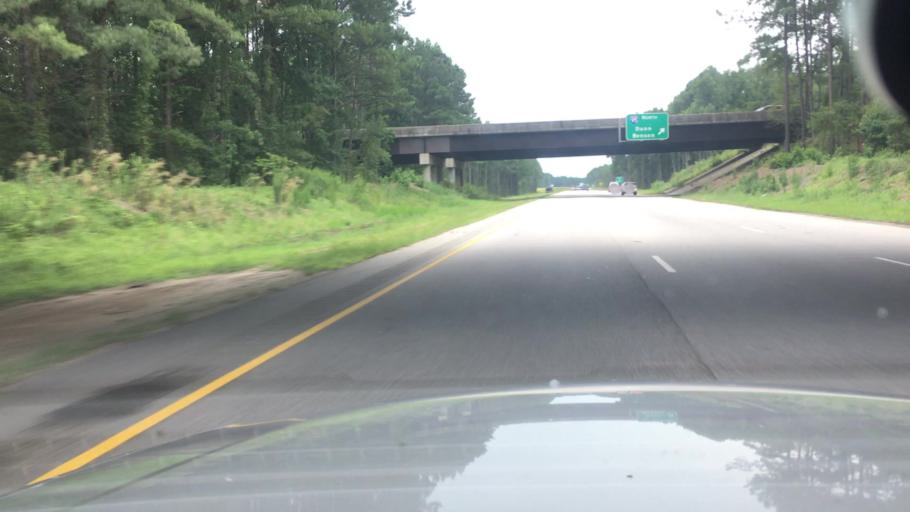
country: US
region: North Carolina
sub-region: Cumberland County
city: Fayetteville
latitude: 34.9770
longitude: -78.8573
